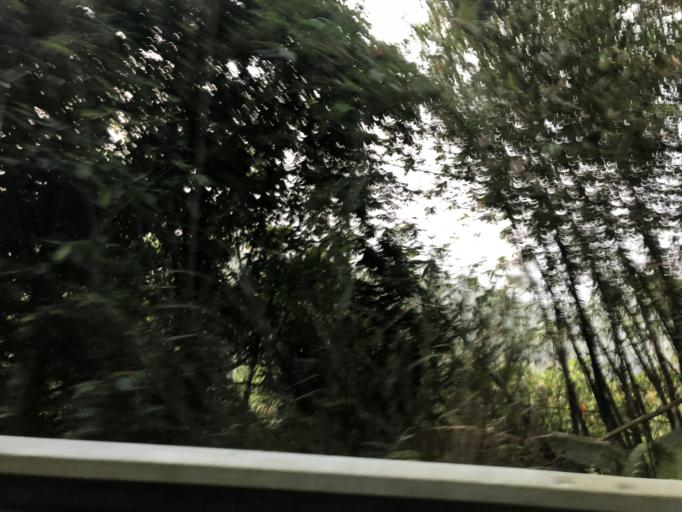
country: TW
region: Taipei
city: Taipei
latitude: 25.1463
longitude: 121.6120
